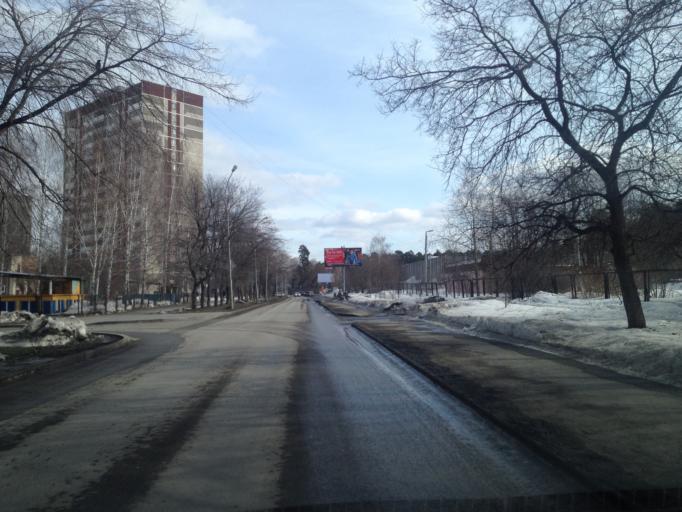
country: RU
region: Sverdlovsk
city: Sovkhoznyy
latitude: 56.7958
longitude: 60.5914
